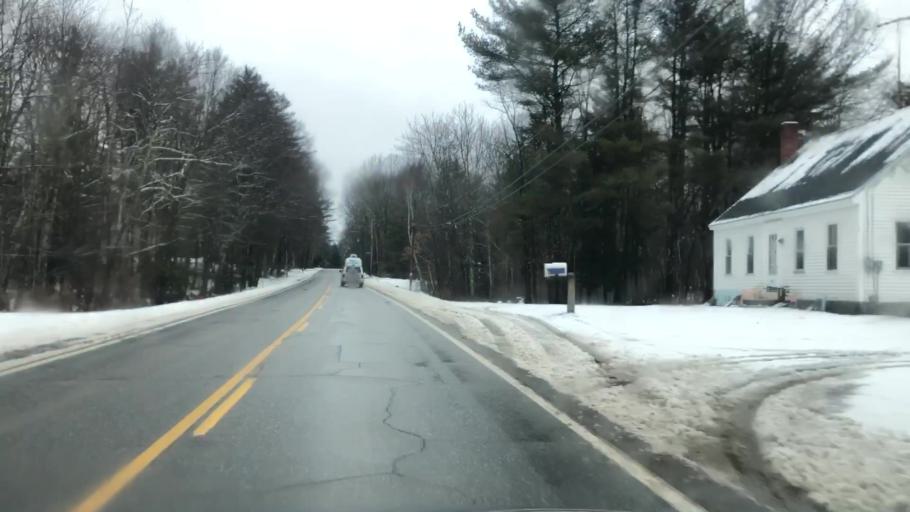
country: US
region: New Hampshire
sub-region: Hillsborough County
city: New Boston
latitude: 43.0201
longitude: -71.6905
